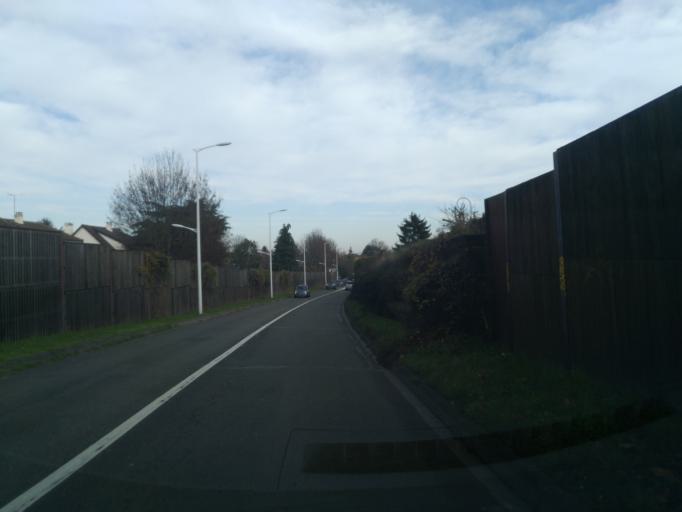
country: FR
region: Ile-de-France
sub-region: Departement des Yvelines
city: Mareil-Marly
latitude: 48.8844
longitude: 2.0705
